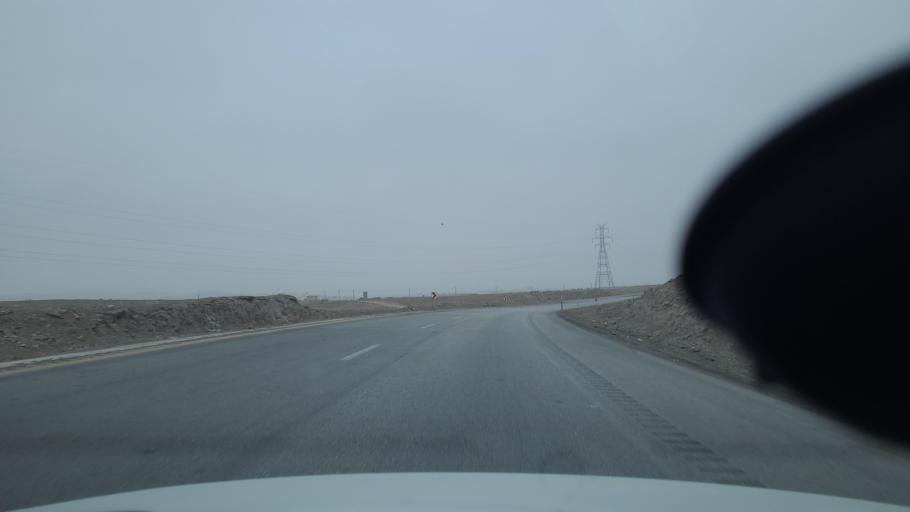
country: IR
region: Razavi Khorasan
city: Fariman
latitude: 35.9782
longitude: 59.7488
